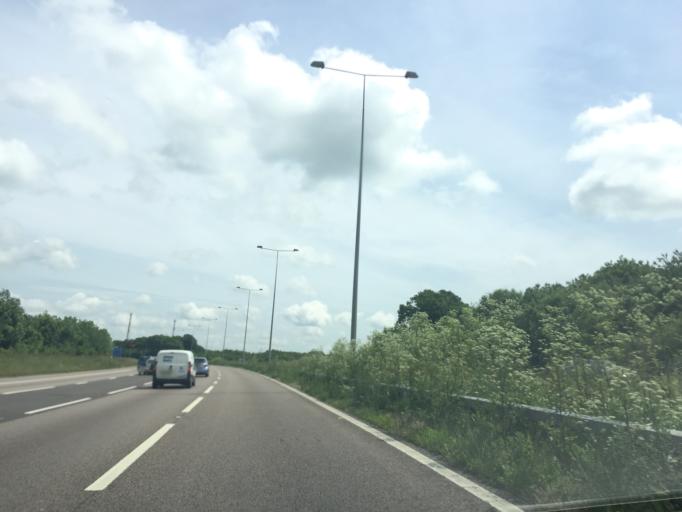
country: GB
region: England
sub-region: Kent
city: Boxley
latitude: 51.3287
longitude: 0.5170
